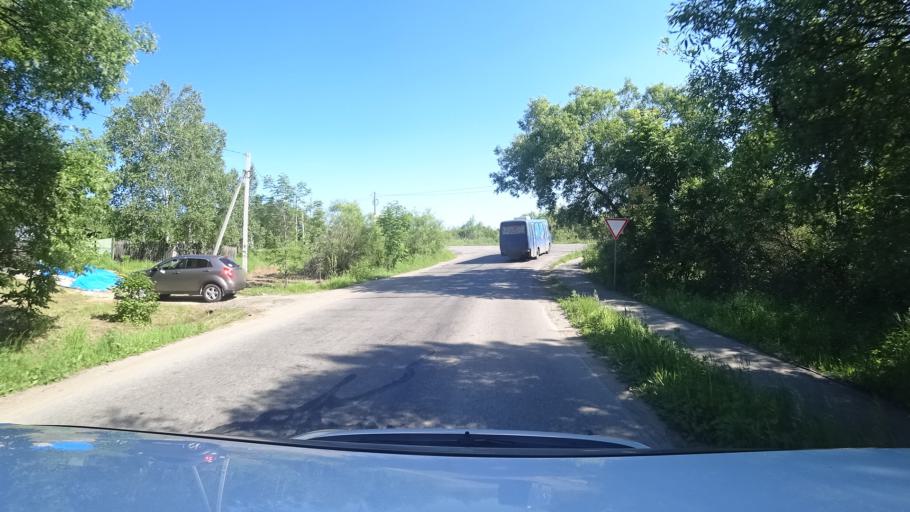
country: RU
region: Khabarovsk Krai
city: Topolevo
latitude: 48.5490
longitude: 135.1910
